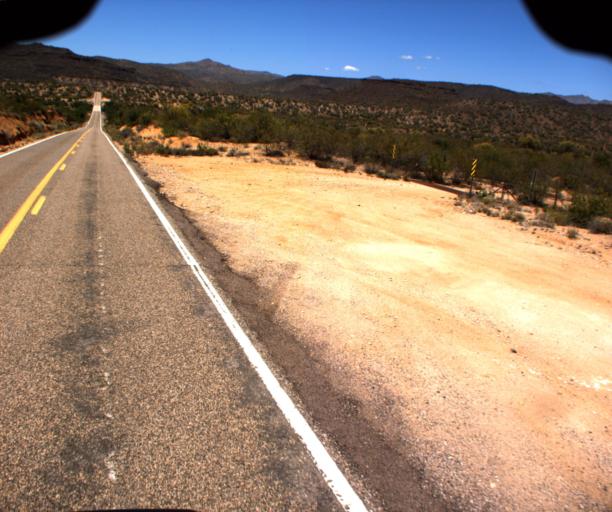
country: US
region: Arizona
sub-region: Yavapai County
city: Bagdad
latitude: 34.4767
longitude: -113.0566
